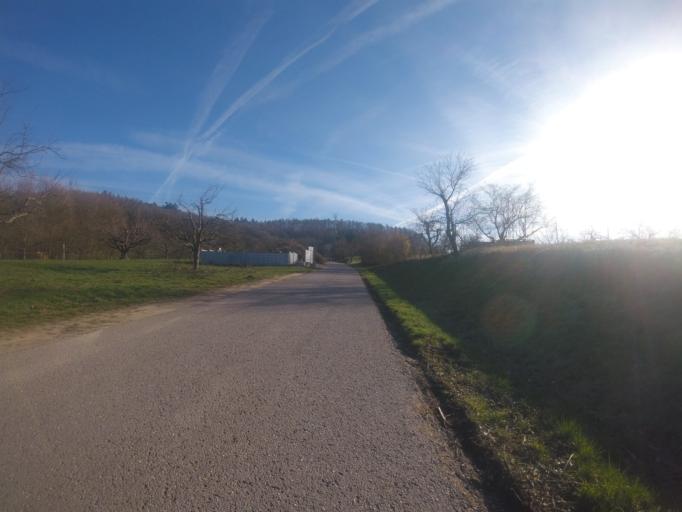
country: DE
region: Baden-Wuerttemberg
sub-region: Regierungsbezirk Stuttgart
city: Oberstenfeld
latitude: 49.0394
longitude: 9.3442
